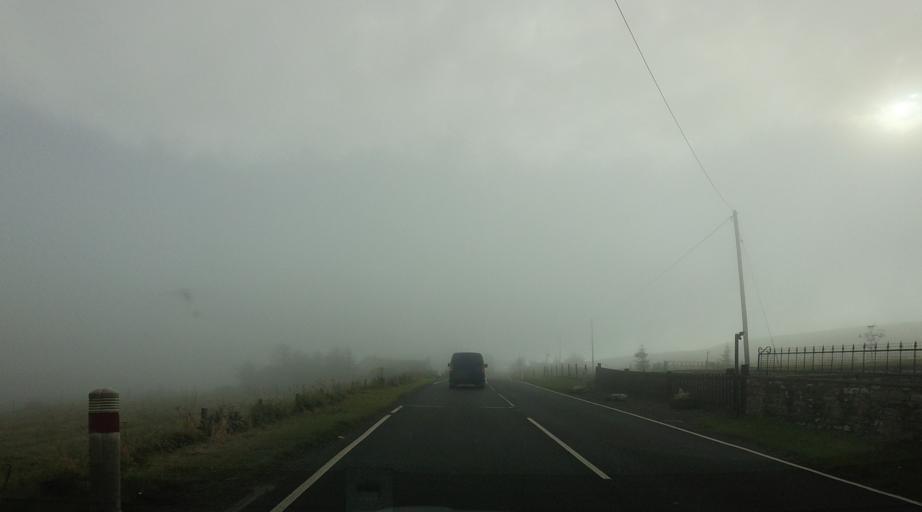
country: GB
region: Scotland
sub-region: Highland
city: Thurso
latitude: 58.2118
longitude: -3.4793
